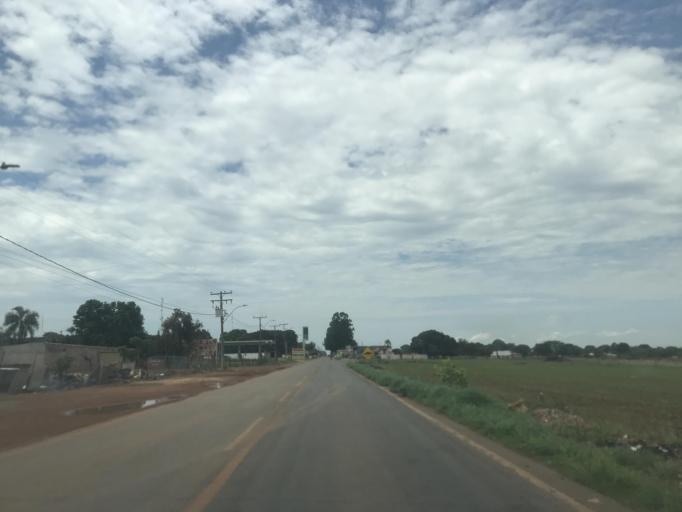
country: BR
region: Goias
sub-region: Luziania
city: Luziania
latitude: -16.3098
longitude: -48.0138
